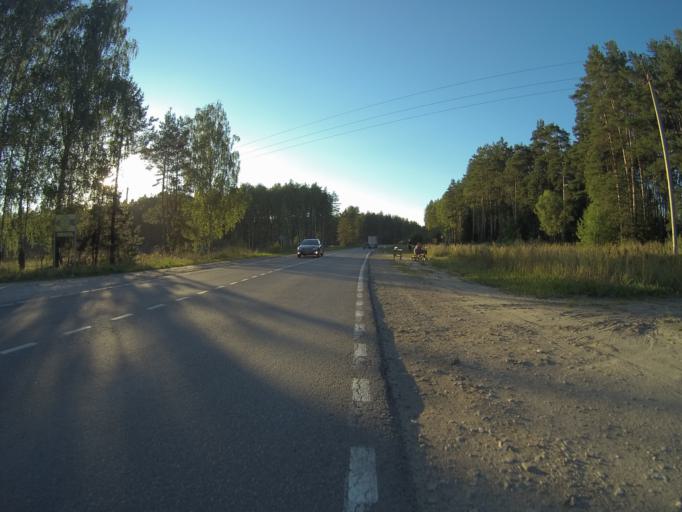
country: RU
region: Vladimir
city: Anopino
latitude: 55.7081
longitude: 40.7311
